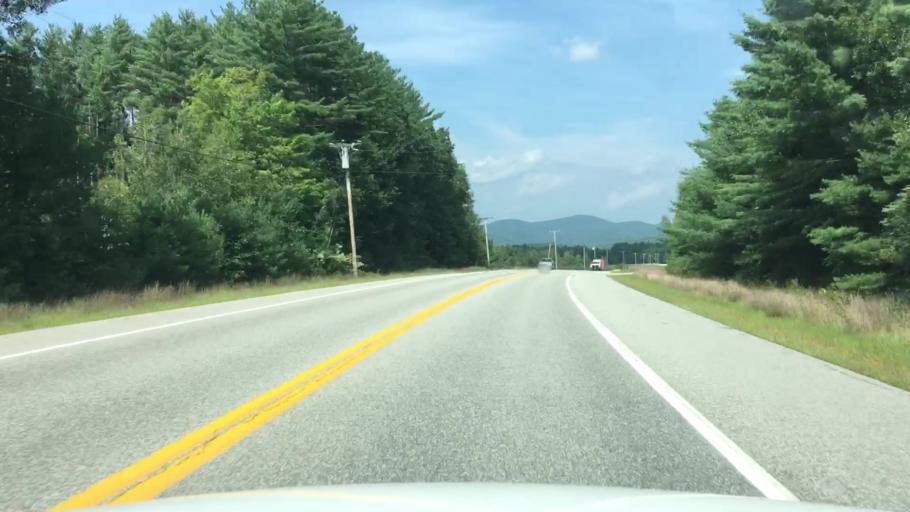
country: US
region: Maine
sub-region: Oxford County
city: Canton
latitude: 44.4587
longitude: -70.3202
